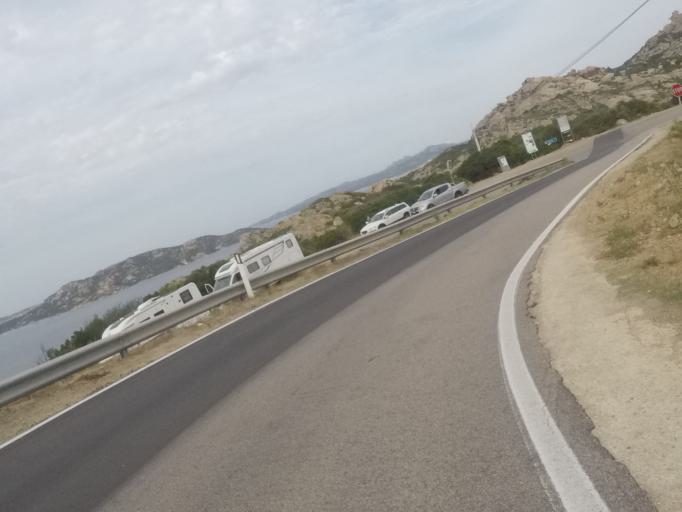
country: IT
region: Sardinia
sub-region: Provincia di Olbia-Tempio
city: Palau
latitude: 41.1718
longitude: 9.4036
